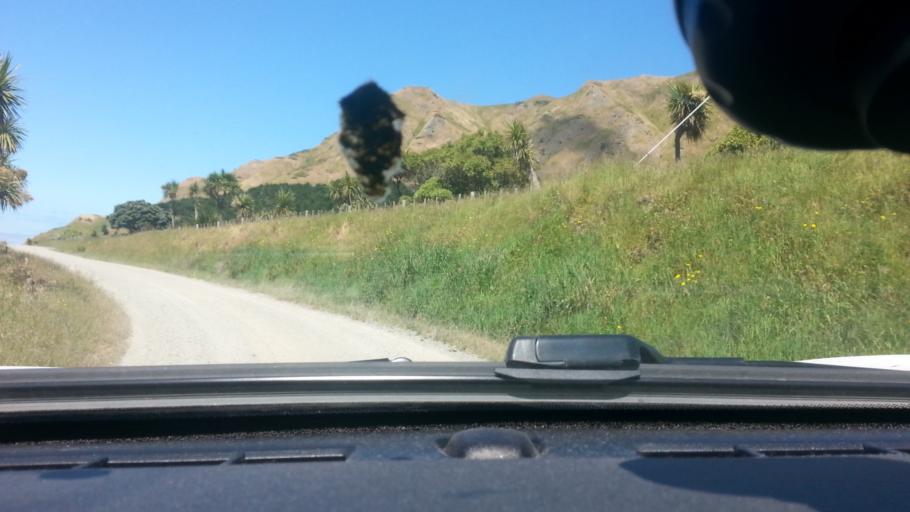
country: NZ
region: Wellington
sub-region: South Wairarapa District
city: Waipawa
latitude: -41.4803
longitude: 175.5763
